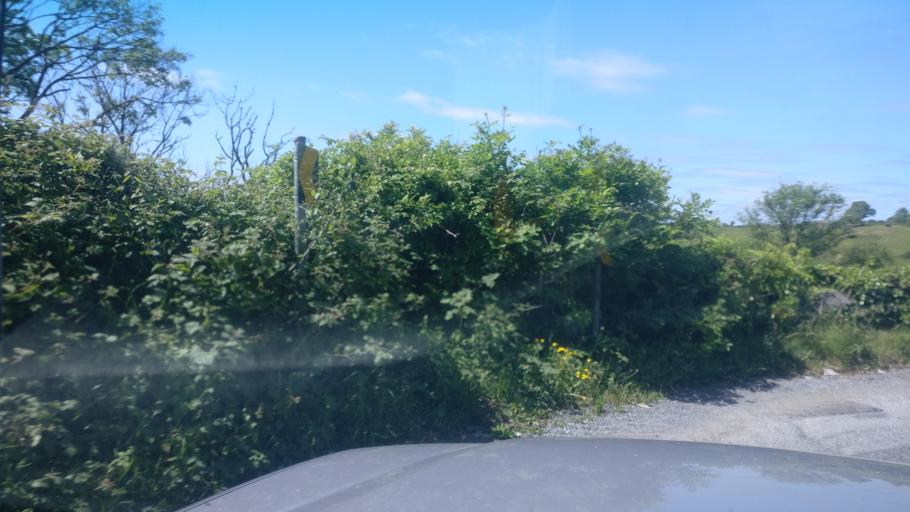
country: IE
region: Connaught
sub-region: County Galway
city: Gort
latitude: 53.0915
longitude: -8.8061
